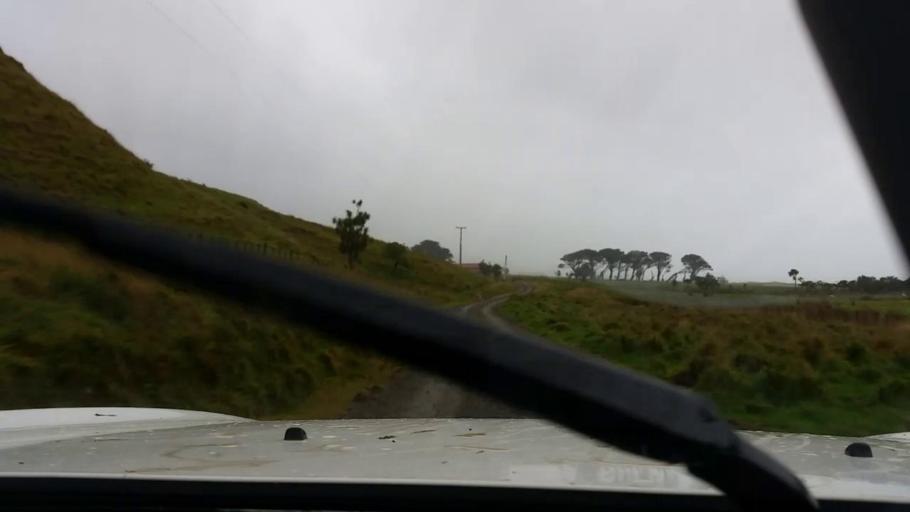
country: NZ
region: Wellington
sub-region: Masterton District
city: Masterton
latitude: -41.2644
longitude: 175.8915
